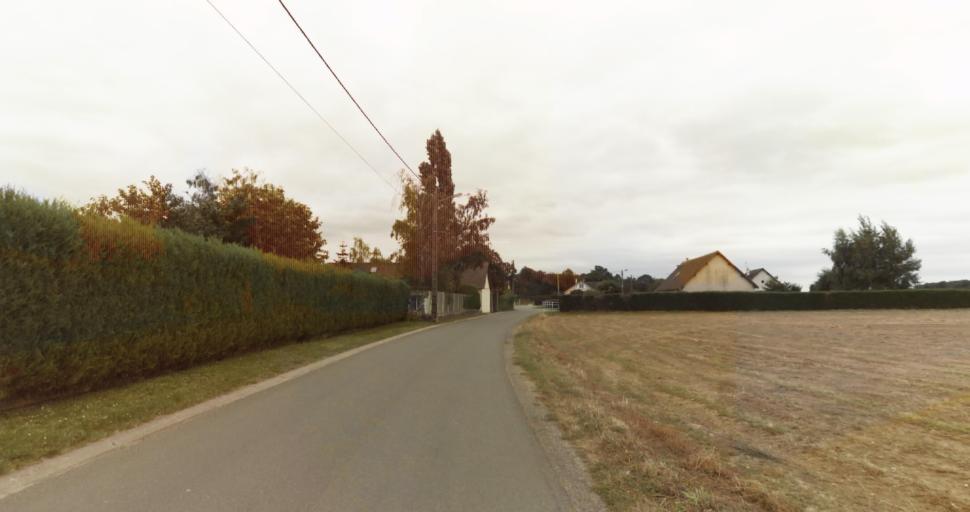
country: FR
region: Haute-Normandie
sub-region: Departement de l'Eure
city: Evreux
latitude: 48.9737
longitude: 1.2343
